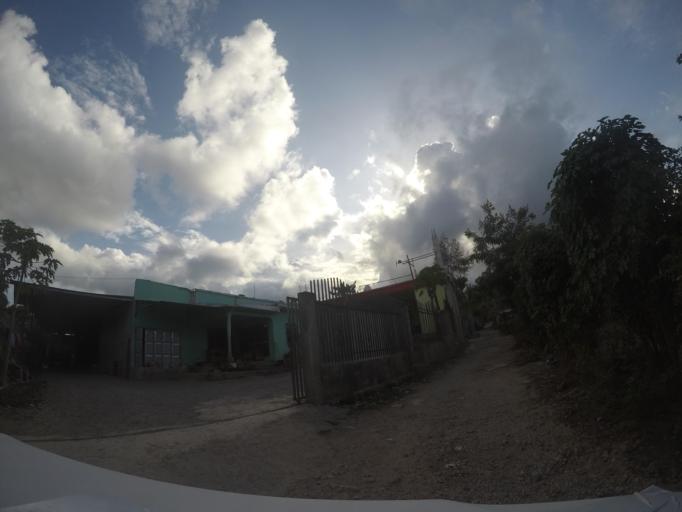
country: TL
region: Baucau
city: Baucau
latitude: -8.4778
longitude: 126.4571
